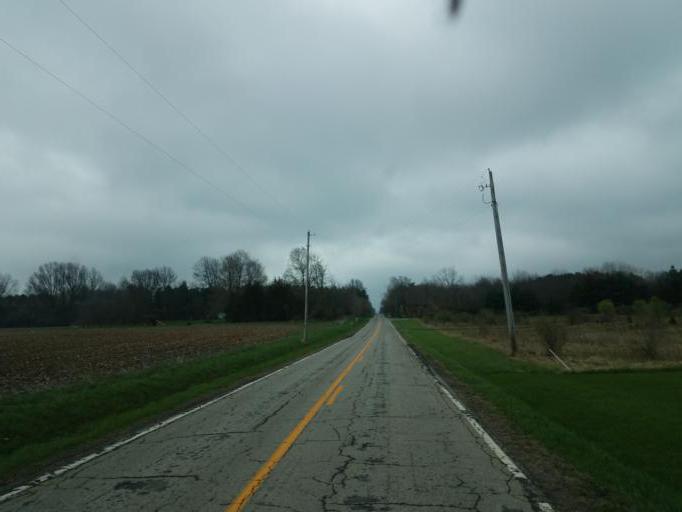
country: US
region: Ohio
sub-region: Crawford County
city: Crestline
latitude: 40.7331
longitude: -82.7048
